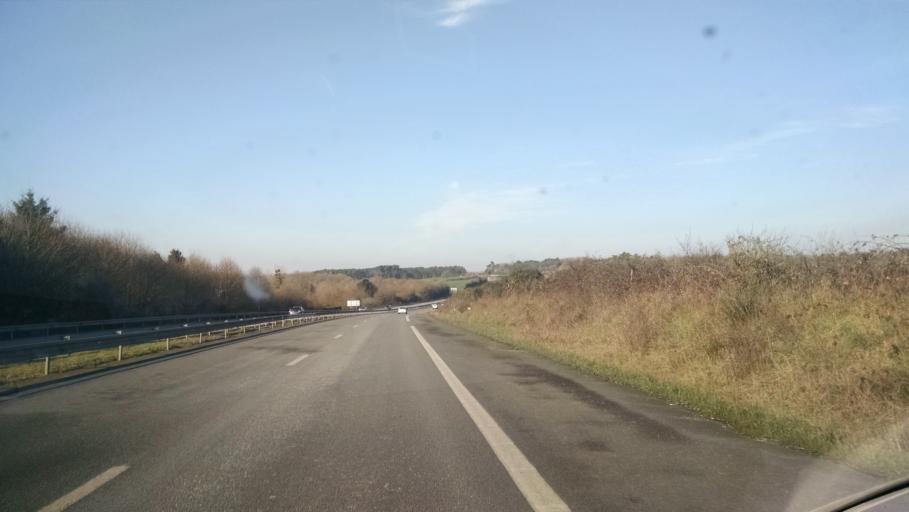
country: FR
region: Brittany
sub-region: Departement du Morbihan
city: Ambon
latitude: 47.5927
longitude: -2.5612
